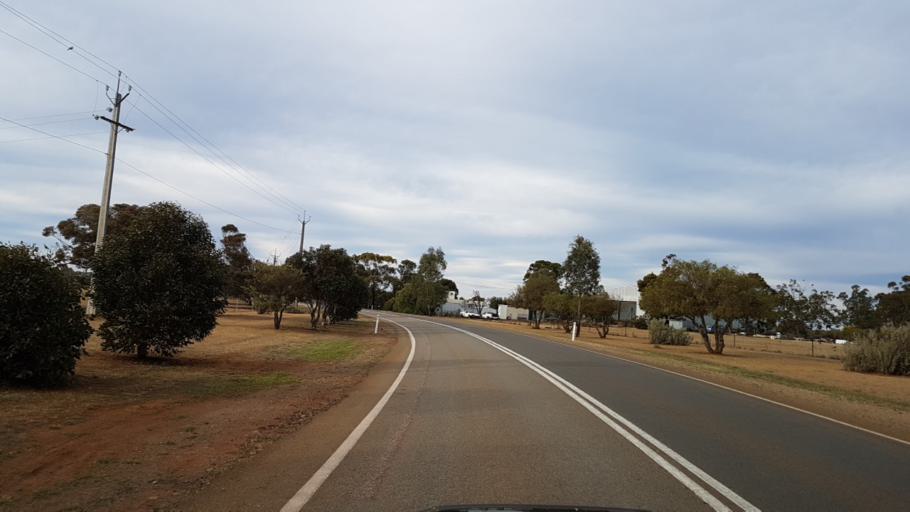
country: AU
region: South Australia
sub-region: Peterborough
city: Peterborough
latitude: -32.9787
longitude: 138.8190
